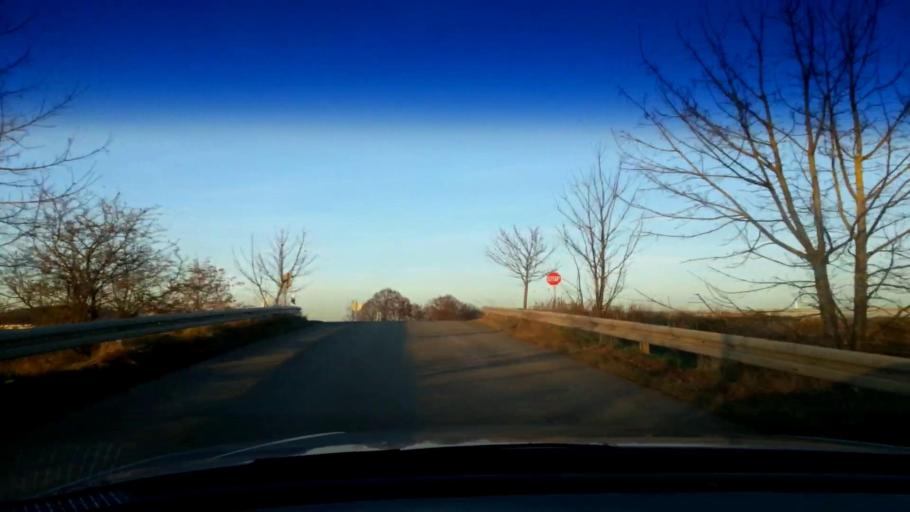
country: DE
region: Bavaria
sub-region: Upper Franconia
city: Ebensfeld
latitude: 50.0604
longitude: 10.9491
